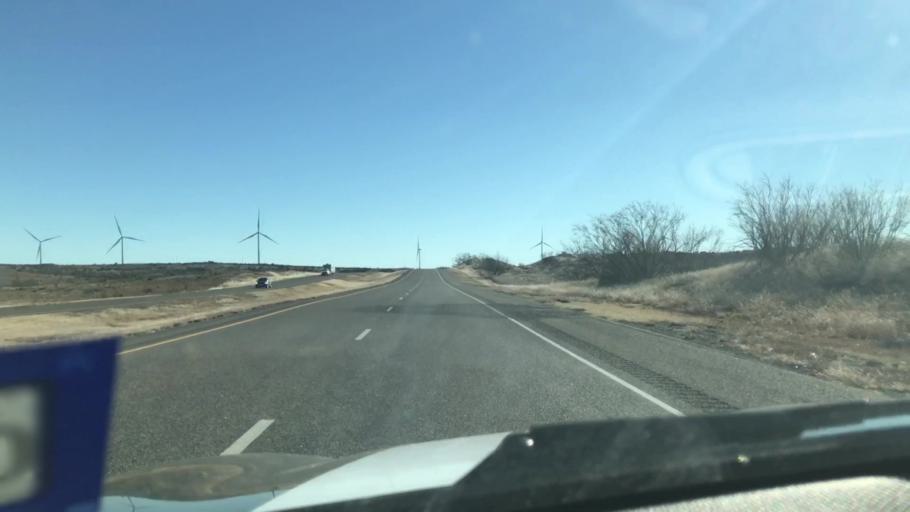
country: US
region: Texas
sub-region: Scurry County
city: Snyder
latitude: 32.9049
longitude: -101.0569
